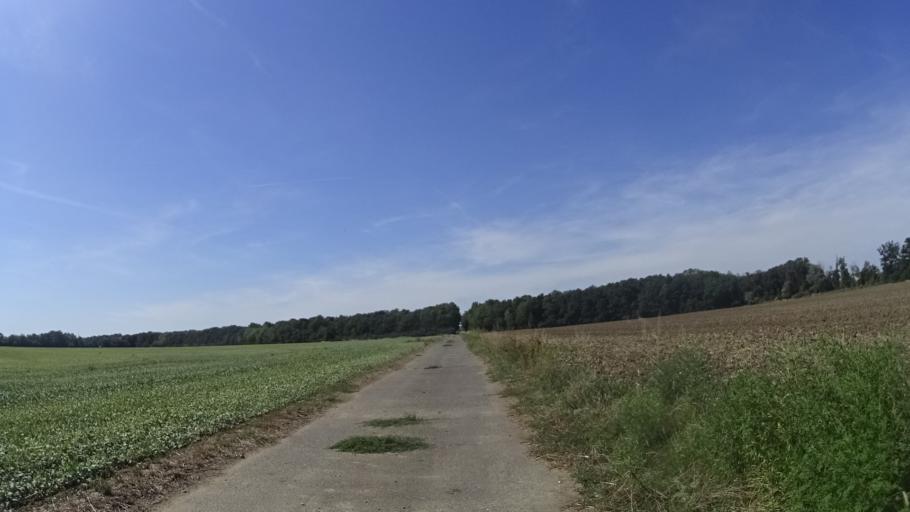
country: AT
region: Lower Austria
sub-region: Politischer Bezirk Ganserndorf
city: Angern an der March
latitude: 48.3680
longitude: 16.8626
